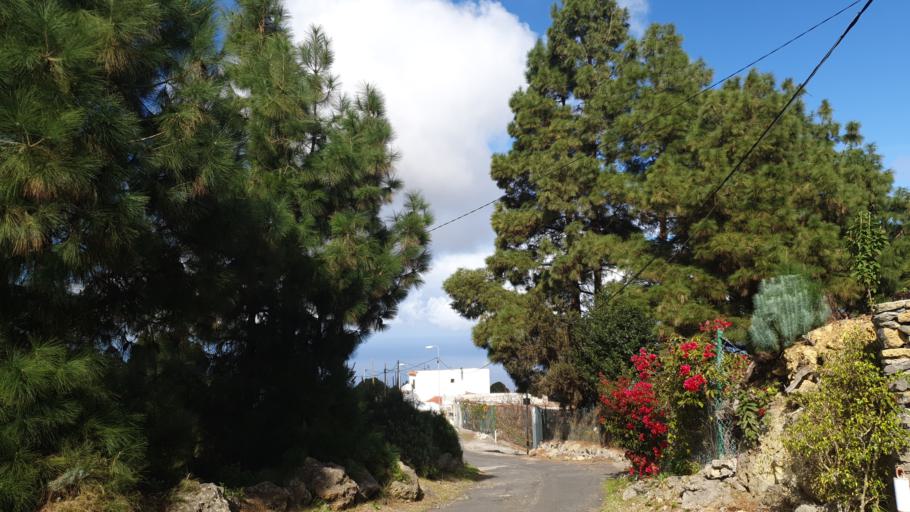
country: ES
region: Canary Islands
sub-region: Provincia de Santa Cruz de Tenerife
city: La Guancha
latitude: 28.3527
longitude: -16.6856
